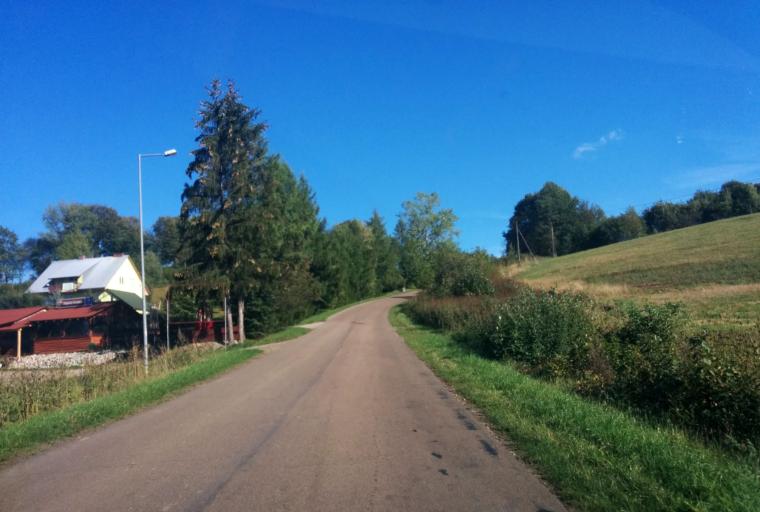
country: PL
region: Subcarpathian Voivodeship
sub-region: Powiat leski
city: Polanczyk
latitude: 49.3042
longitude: 22.4180
